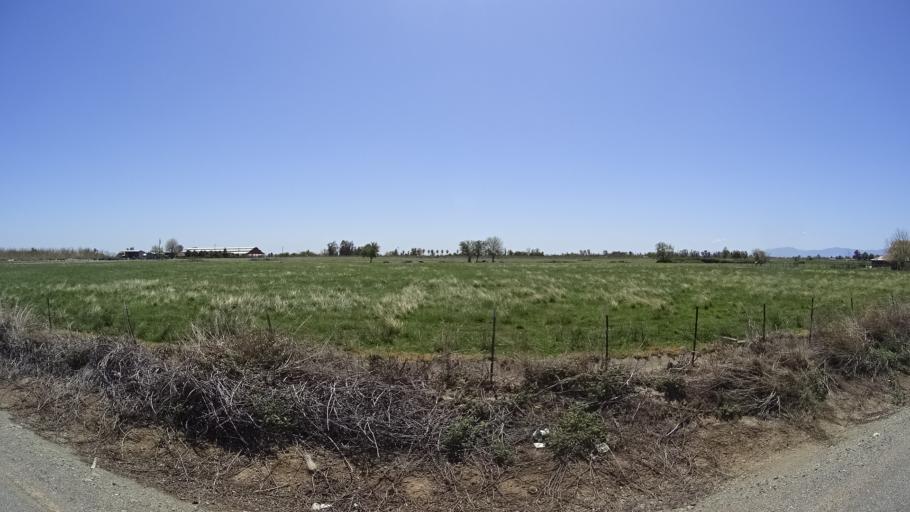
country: US
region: California
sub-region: Glenn County
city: Orland
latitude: 39.7945
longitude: -122.1878
